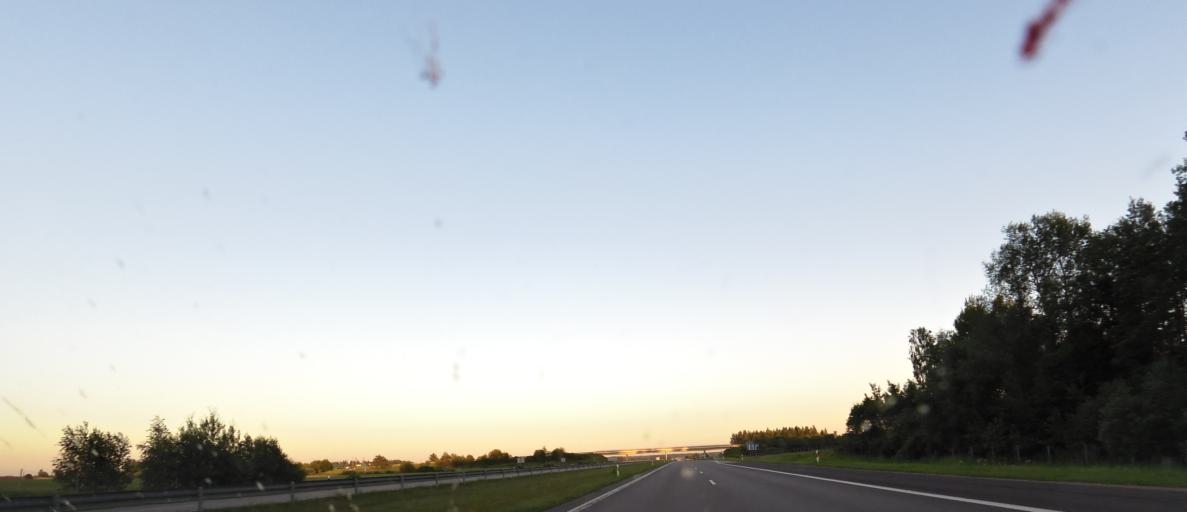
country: LT
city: Sirvintos
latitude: 54.9504
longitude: 24.9637
